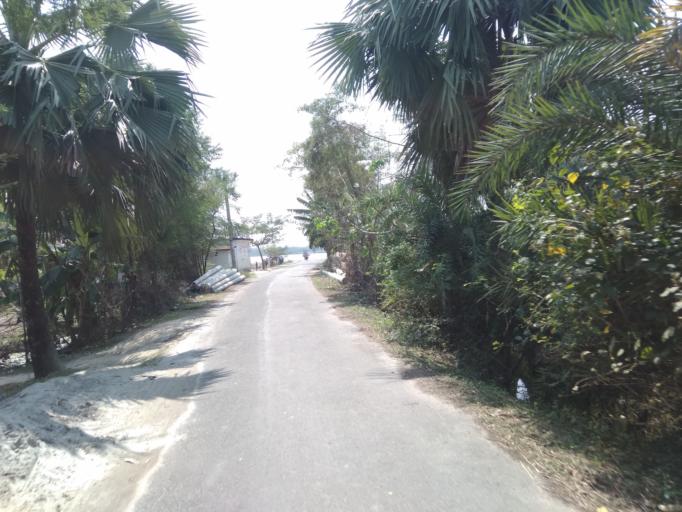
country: BD
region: Khulna
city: Satkhira
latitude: 22.4024
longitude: 89.2133
